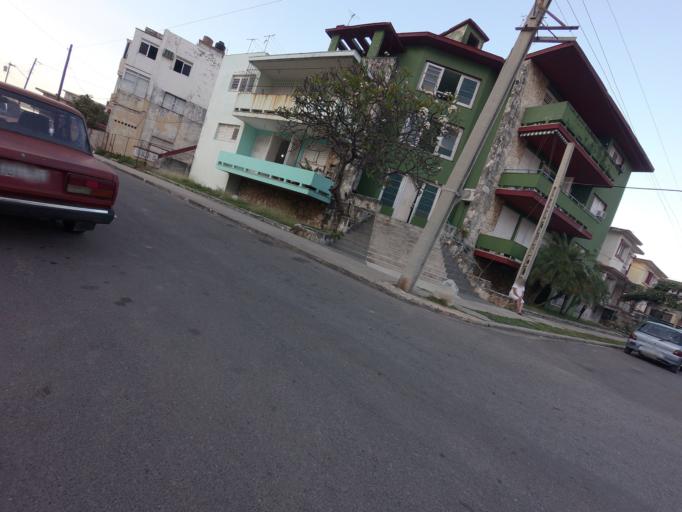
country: CU
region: La Habana
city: Cerro
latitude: 23.0929
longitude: -82.4578
